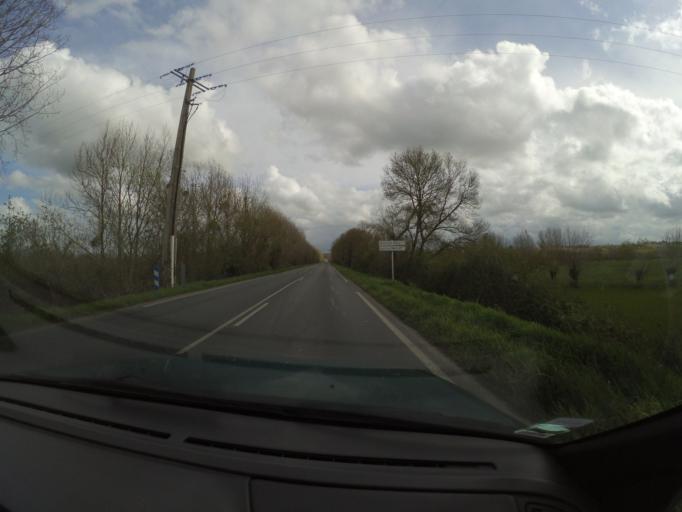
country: FR
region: Pays de la Loire
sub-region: Departement de la Loire-Atlantique
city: Ancenis
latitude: 47.3549
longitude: -1.1721
